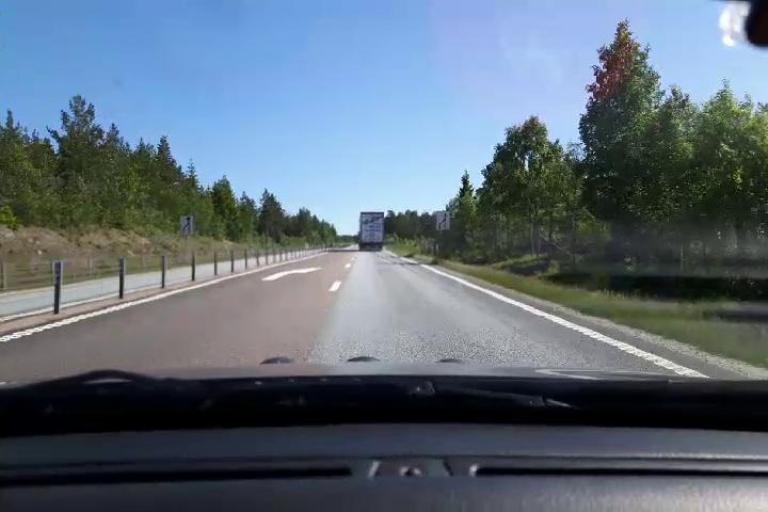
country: SE
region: Gaevleborg
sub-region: Soderhamns Kommun
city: Soderhamn
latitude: 61.2658
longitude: 17.0299
